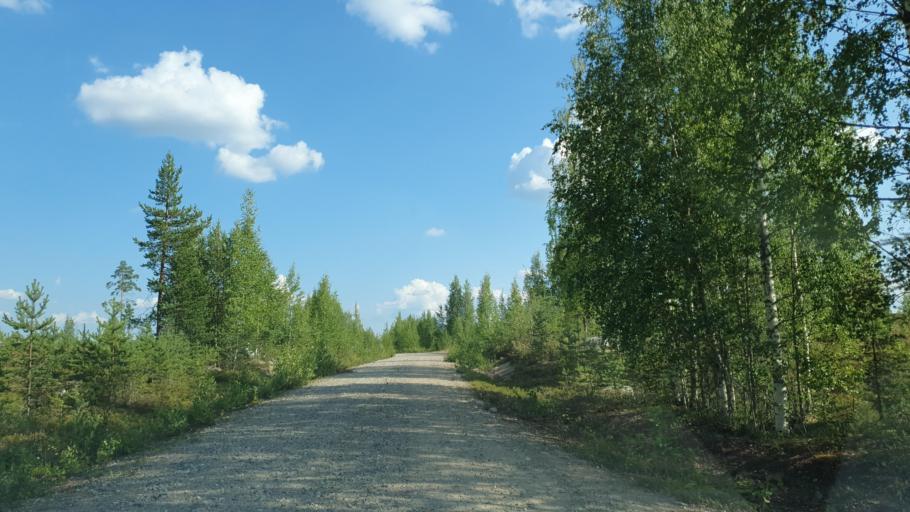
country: FI
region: Kainuu
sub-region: Kehys-Kainuu
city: Kuhmo
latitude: 63.9514
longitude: 29.5690
